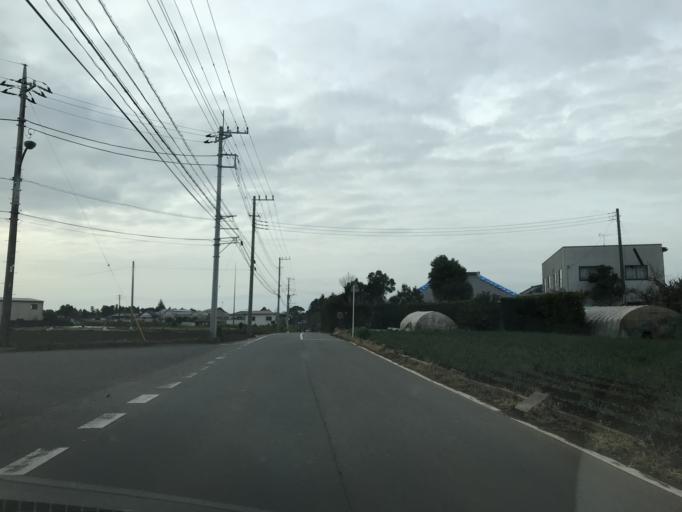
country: JP
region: Chiba
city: Omigawa
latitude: 35.8003
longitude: 140.5795
